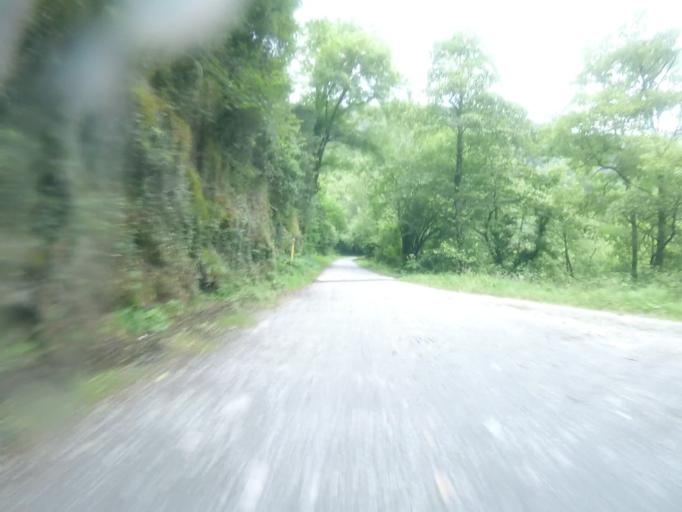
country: ES
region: Navarre
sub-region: Provincia de Navarra
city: Sunbilla
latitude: 43.1996
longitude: -1.6729
